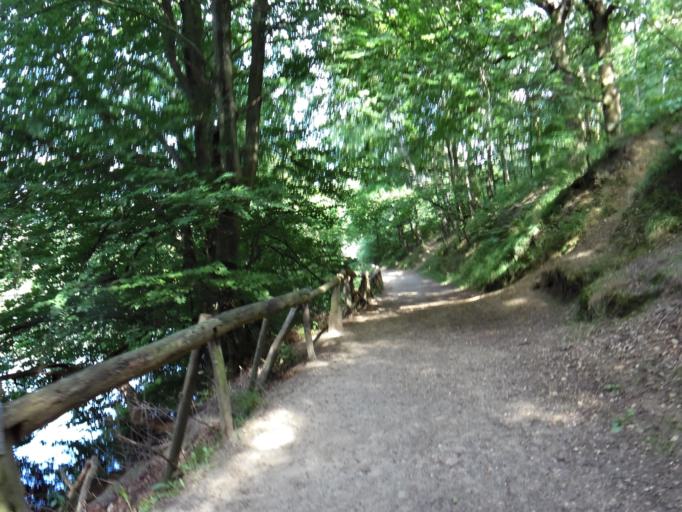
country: DE
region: North Rhine-Westphalia
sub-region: Regierungsbezirk Koln
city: Alsdorf
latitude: 50.8539
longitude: 6.1726
